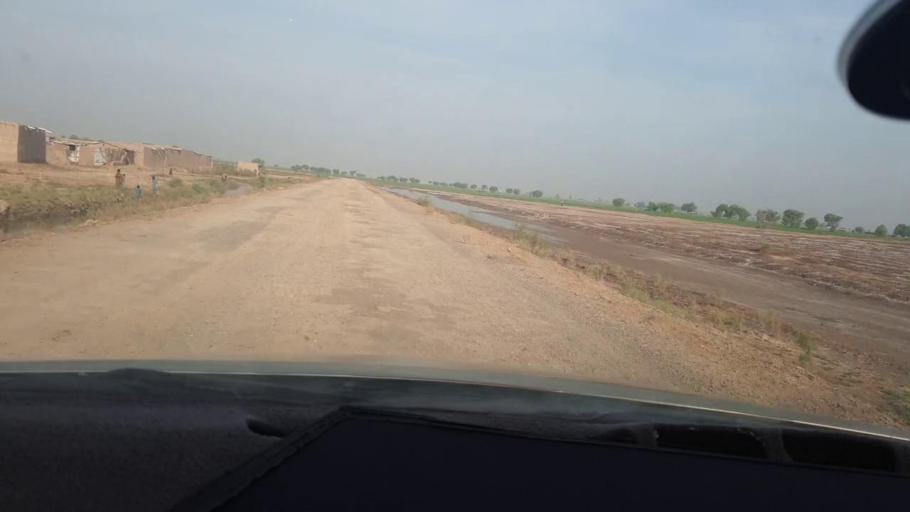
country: PK
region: Sindh
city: Jacobabad
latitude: 28.3355
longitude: 68.4094
